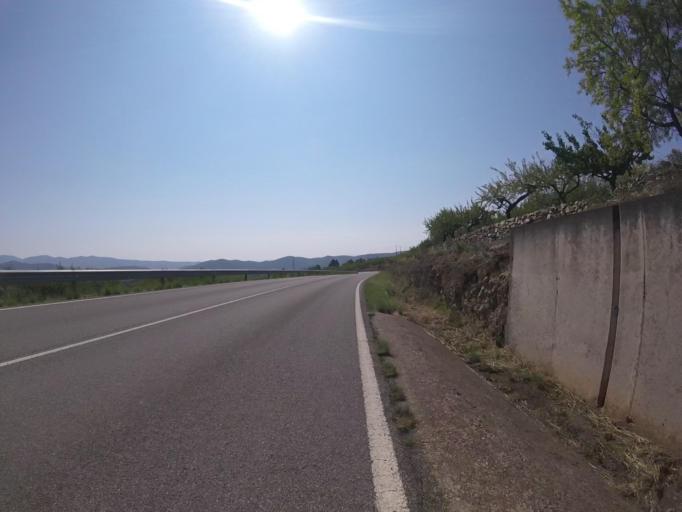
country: ES
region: Valencia
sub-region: Provincia de Castello
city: Adzaneta
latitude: 40.2436
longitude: -0.1925
